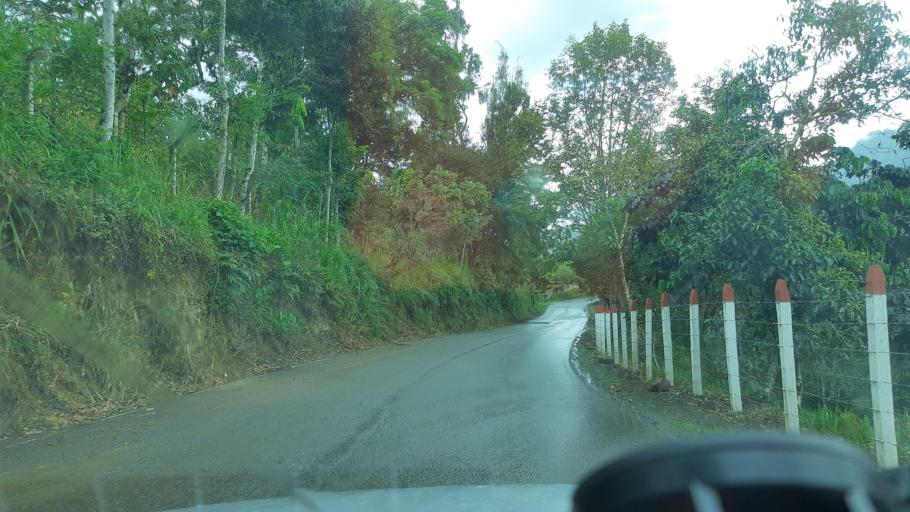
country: CO
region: Boyaca
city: Chinavita
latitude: 5.1490
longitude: -73.3637
